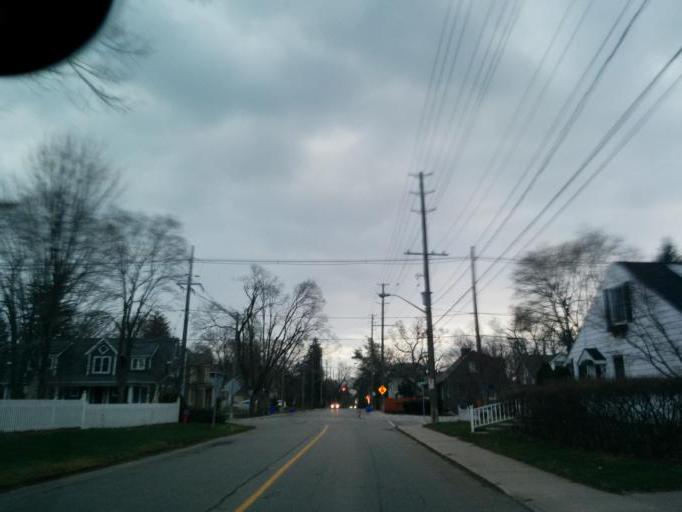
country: CA
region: Ontario
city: Oakville
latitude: 43.4564
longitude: -79.6752
